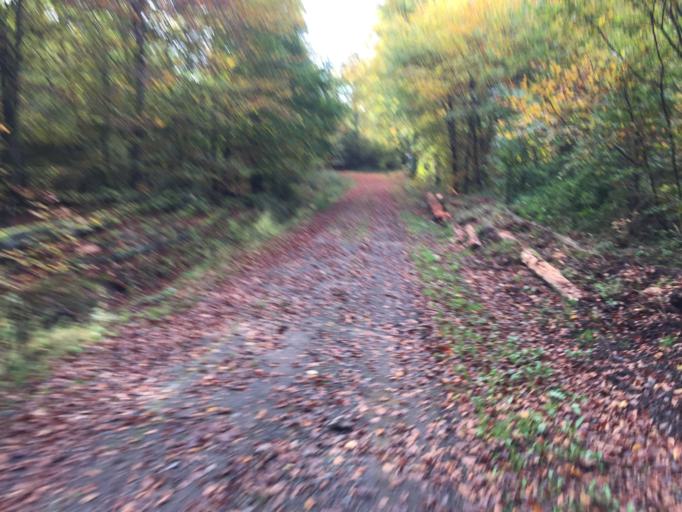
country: DE
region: Hesse
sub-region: Regierungsbezirk Giessen
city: Laubach
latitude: 50.5669
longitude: 8.9900
